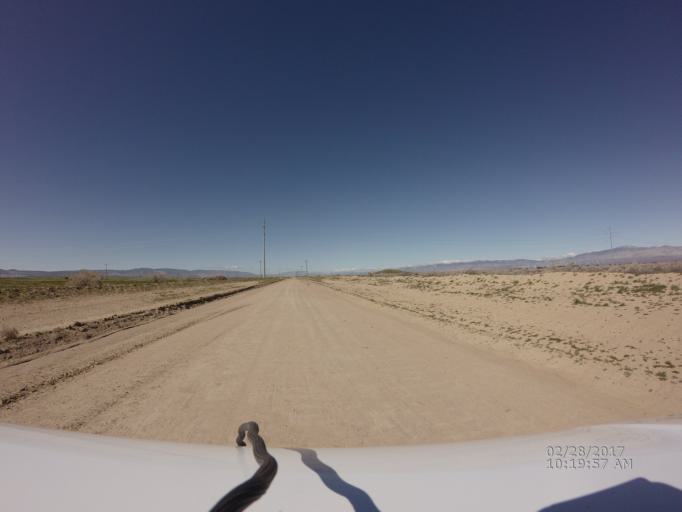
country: US
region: California
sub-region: Kern County
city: Rosamond
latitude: 34.7913
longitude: -118.3155
